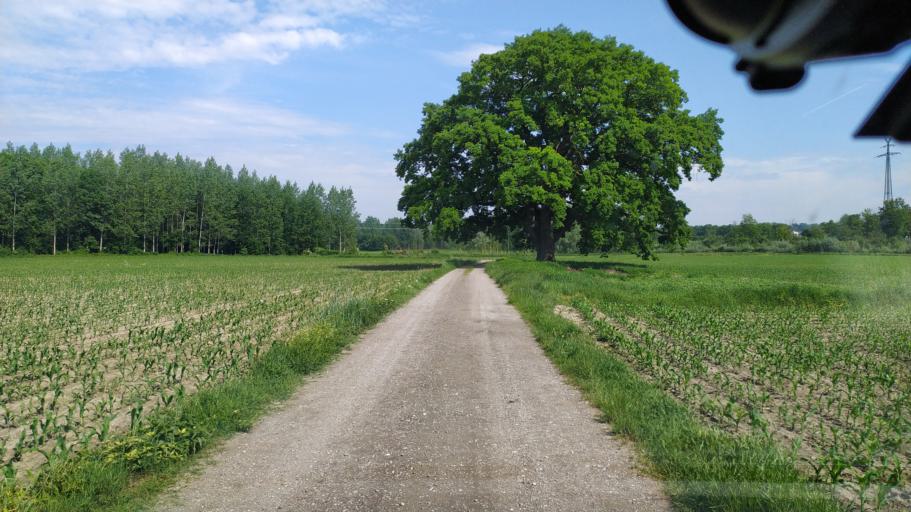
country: AT
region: Lower Austria
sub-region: Politischer Bezirk Amstetten
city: Strengberg
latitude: 48.1732
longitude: 14.6847
